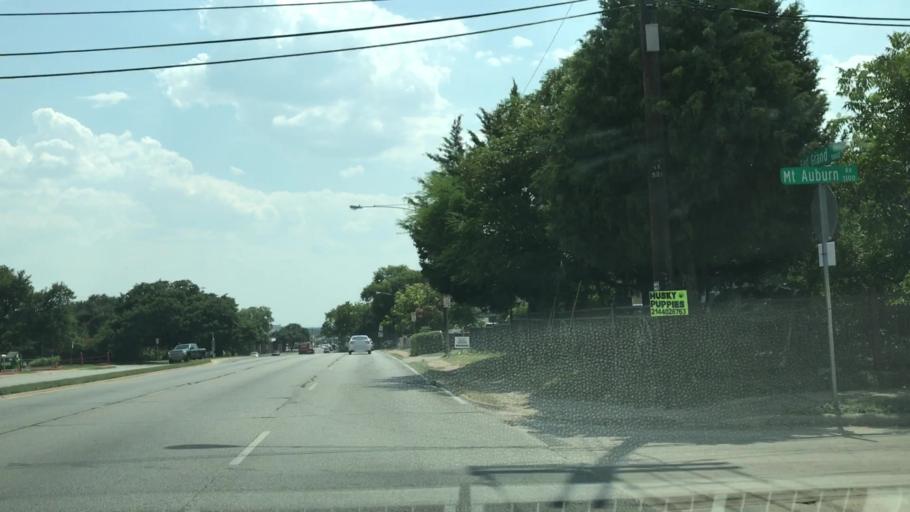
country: US
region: Texas
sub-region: Dallas County
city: Highland Park
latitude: 32.7967
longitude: -96.7444
